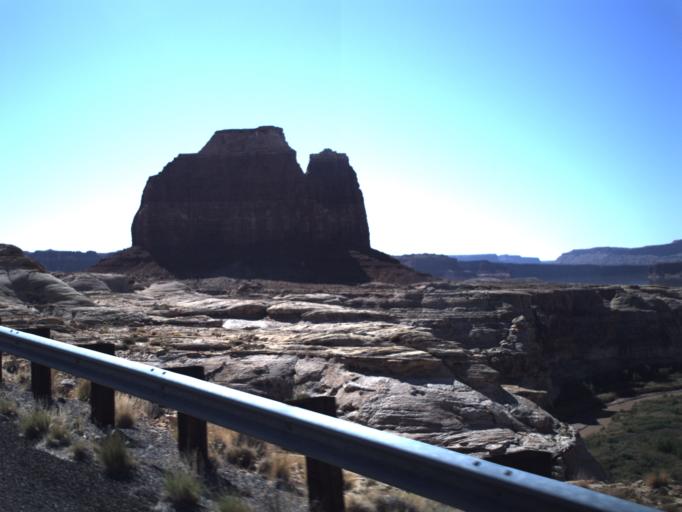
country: US
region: Utah
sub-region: San Juan County
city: Blanding
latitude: 37.9115
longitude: -110.3866
